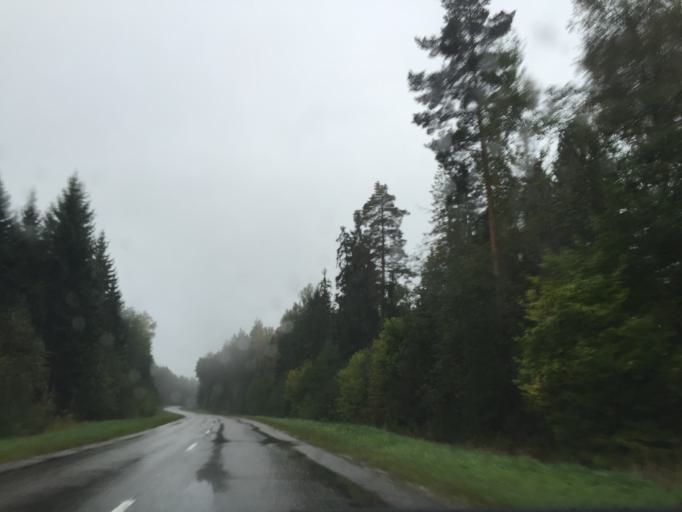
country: LV
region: Ropazu
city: Ropazi
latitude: 57.0256
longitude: 24.6823
